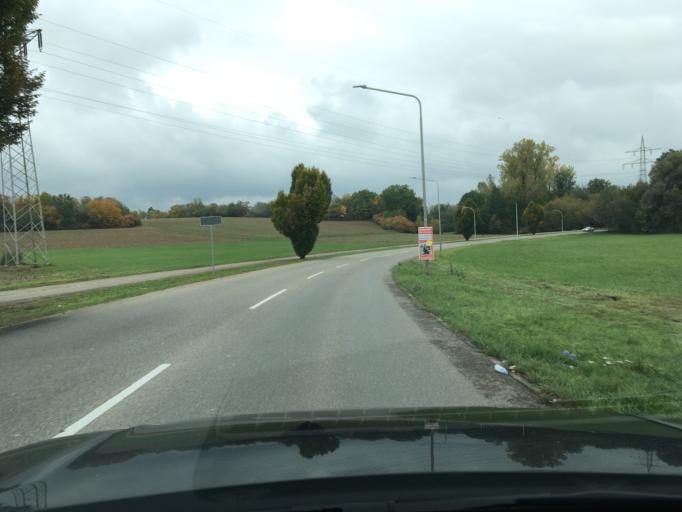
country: DE
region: Baden-Wuerttemberg
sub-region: Tuebingen Region
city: Ofterdingen
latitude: 48.4049
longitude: 9.0342
